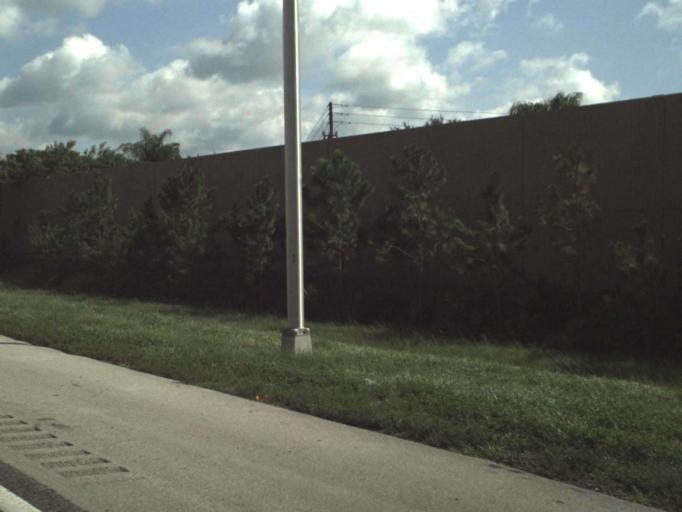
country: US
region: Florida
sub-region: Palm Beach County
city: Limestone Creek
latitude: 26.9034
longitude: -80.1386
